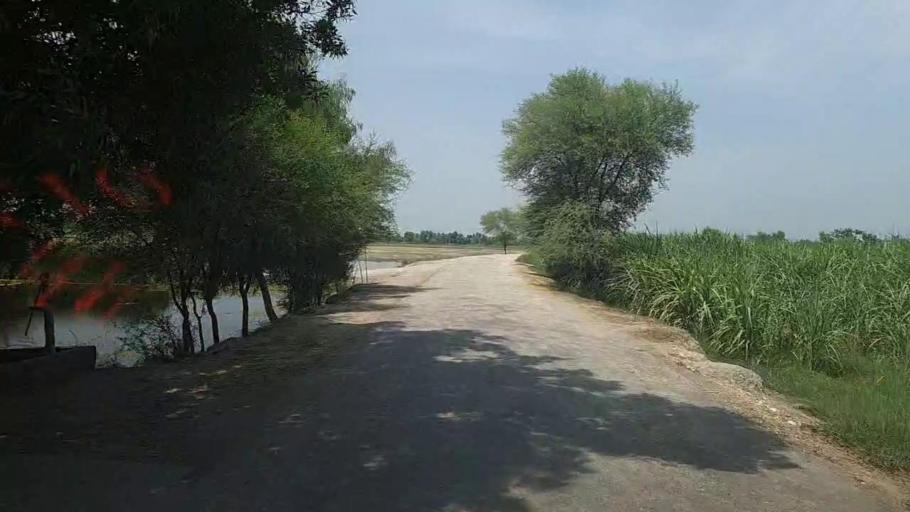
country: PK
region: Sindh
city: Ubauro
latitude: 28.1840
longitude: 69.7694
